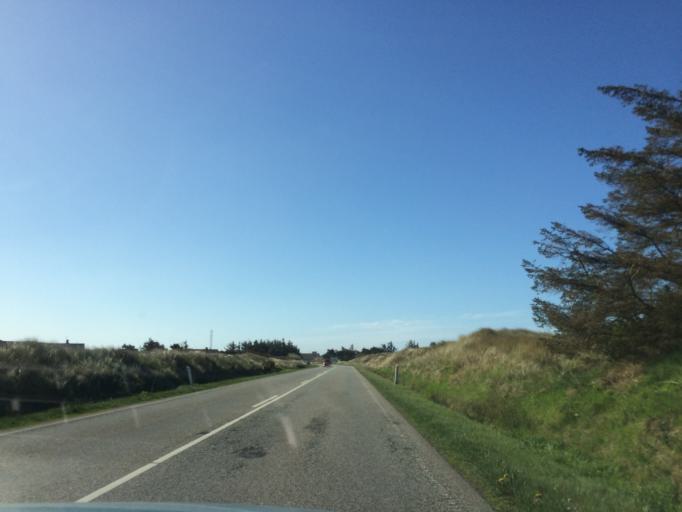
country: DK
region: Central Jutland
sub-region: Ringkobing-Skjern Kommune
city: Hvide Sande
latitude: 56.0242
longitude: 8.1209
